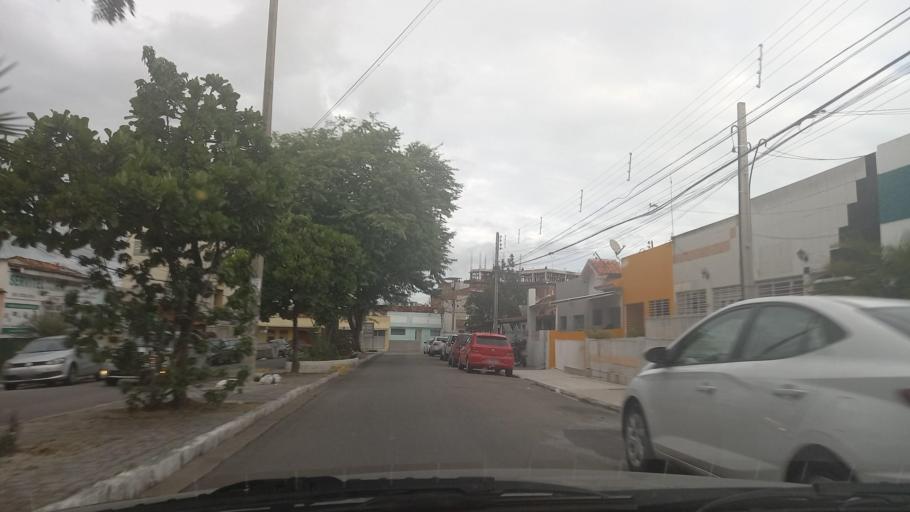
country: BR
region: Pernambuco
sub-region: Caruaru
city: Caruaru
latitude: -8.2813
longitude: -35.9752
